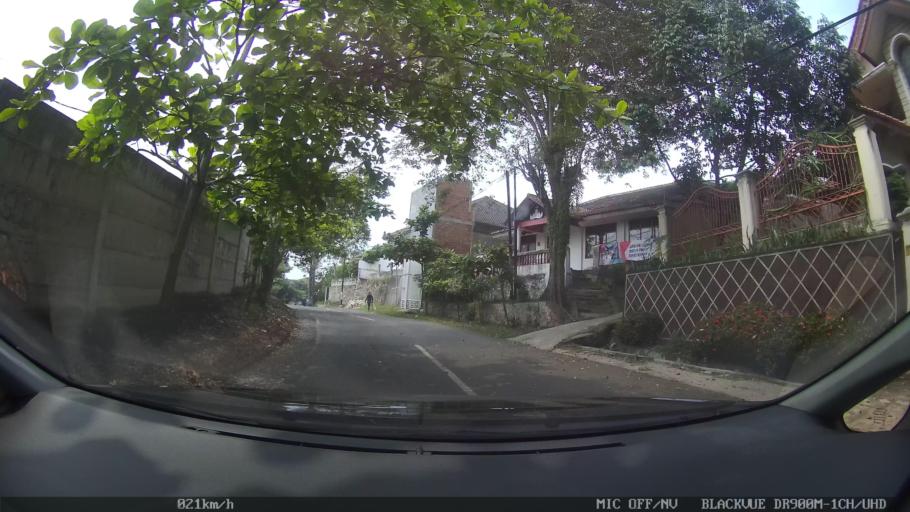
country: ID
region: Lampung
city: Bandarlampung
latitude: -5.4304
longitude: 105.2632
